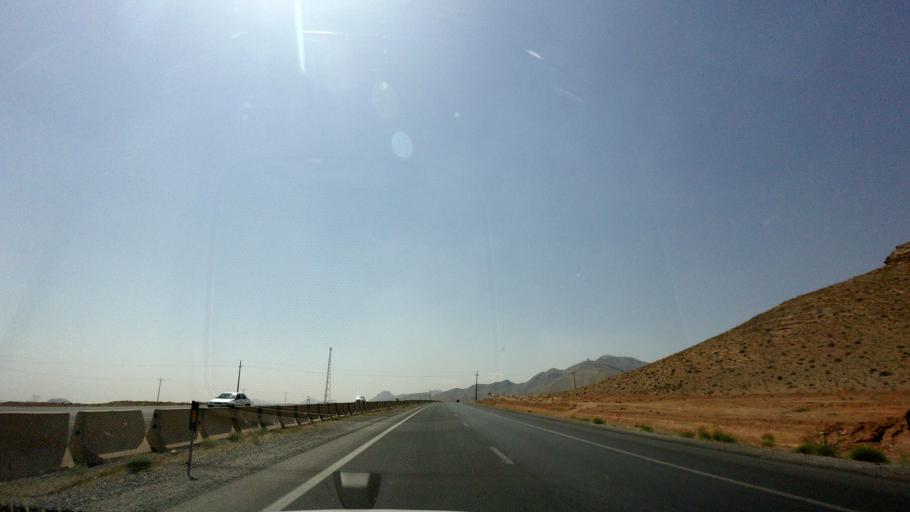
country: IR
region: Isfahan
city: Najafabad
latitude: 32.5713
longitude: 51.2977
